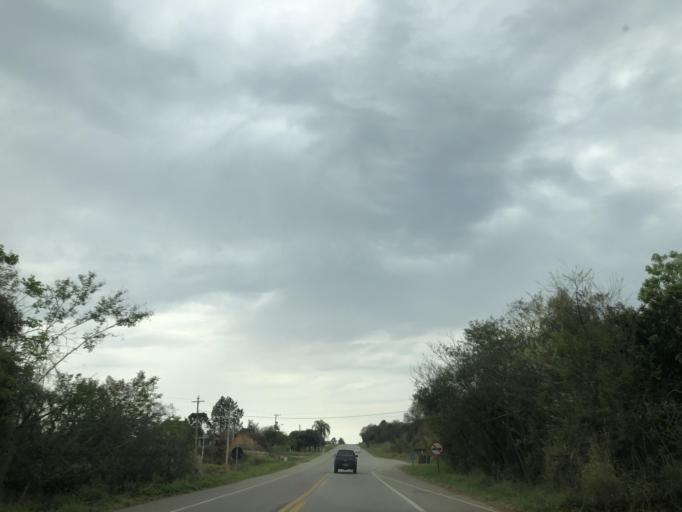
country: BR
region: Sao Paulo
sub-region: Salto De Pirapora
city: Salto de Pirapora
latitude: -23.7063
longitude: -47.6305
